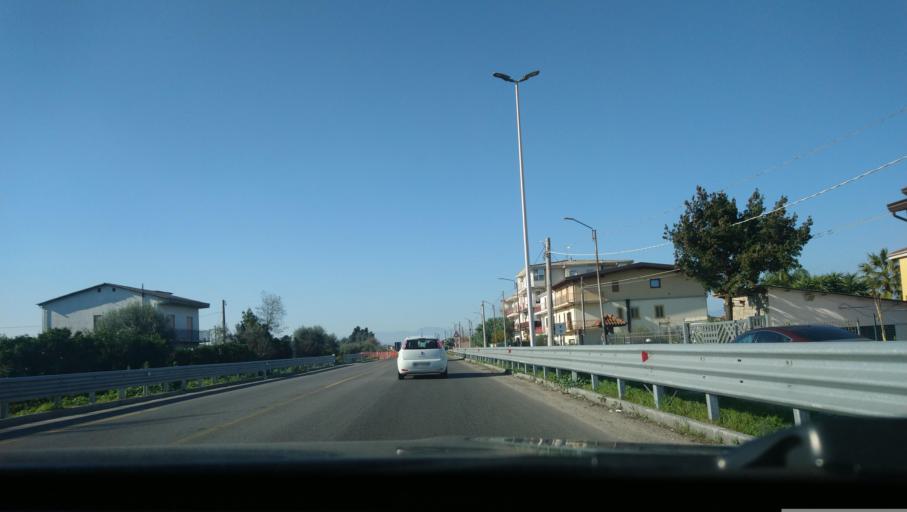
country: IT
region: Calabria
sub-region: Provincia di Cosenza
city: Fabrizio
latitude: 39.6322
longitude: 16.5639
